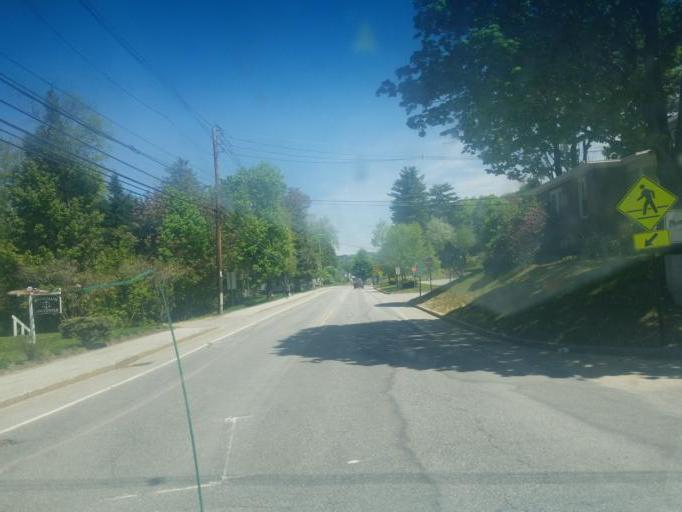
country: US
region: New Hampshire
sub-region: Grafton County
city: Plymouth
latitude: 43.7589
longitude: -71.6961
